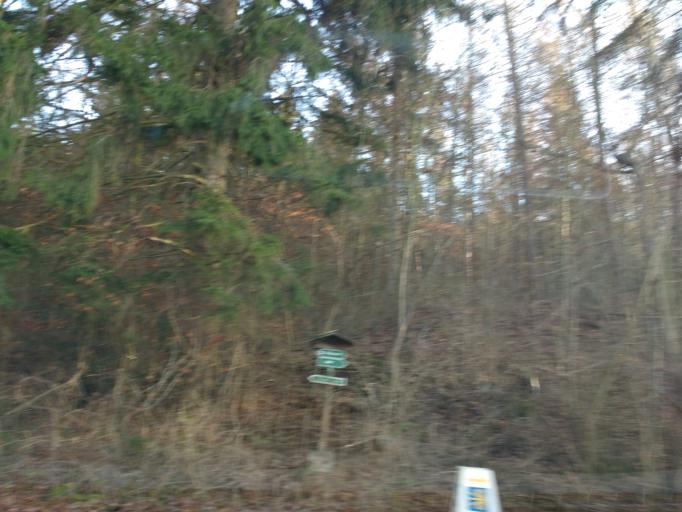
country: DE
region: Thuringia
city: Uder
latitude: 51.3650
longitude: 10.0974
